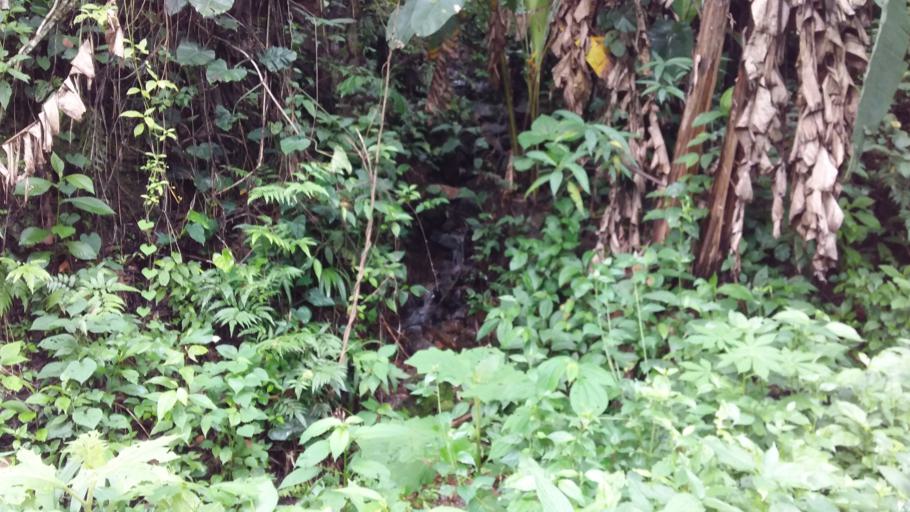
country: CO
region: Casanare
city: Nunchia
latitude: 5.6458
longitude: -72.2954
